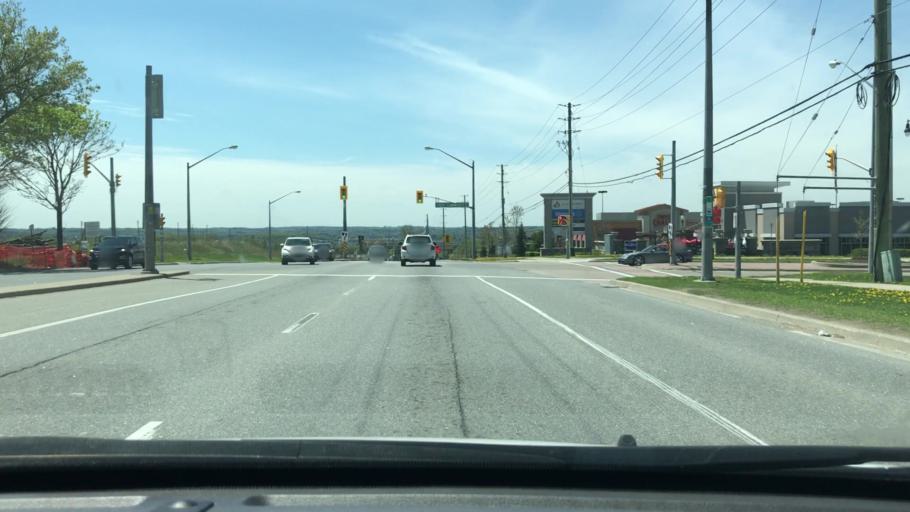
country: CA
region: Ontario
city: Newmarket
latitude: 44.0122
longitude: -79.4138
